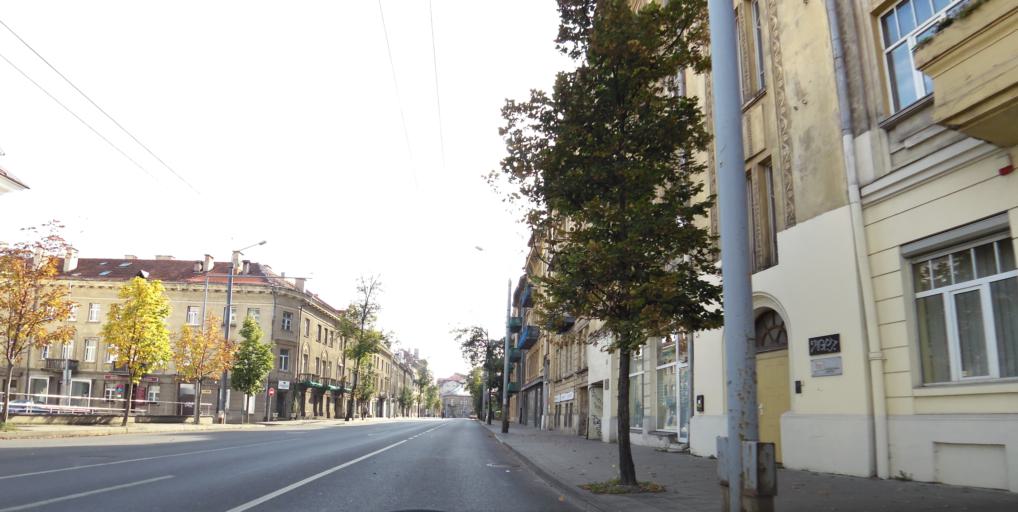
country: LT
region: Vilnius County
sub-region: Vilnius
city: Vilnius
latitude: 54.6859
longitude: 25.2746
